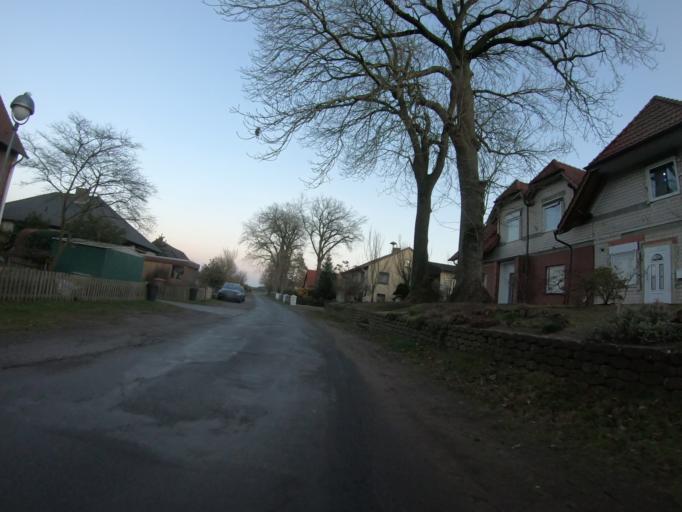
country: DE
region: Lower Saxony
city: Wagenhoff
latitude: 52.4916
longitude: 10.4777
